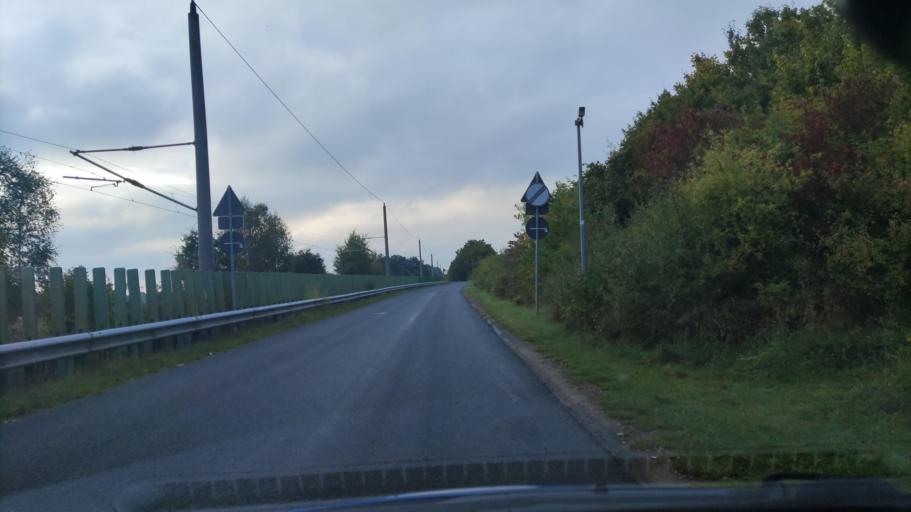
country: DE
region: Lower Saxony
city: Wieren
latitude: 52.8994
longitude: 10.6182
